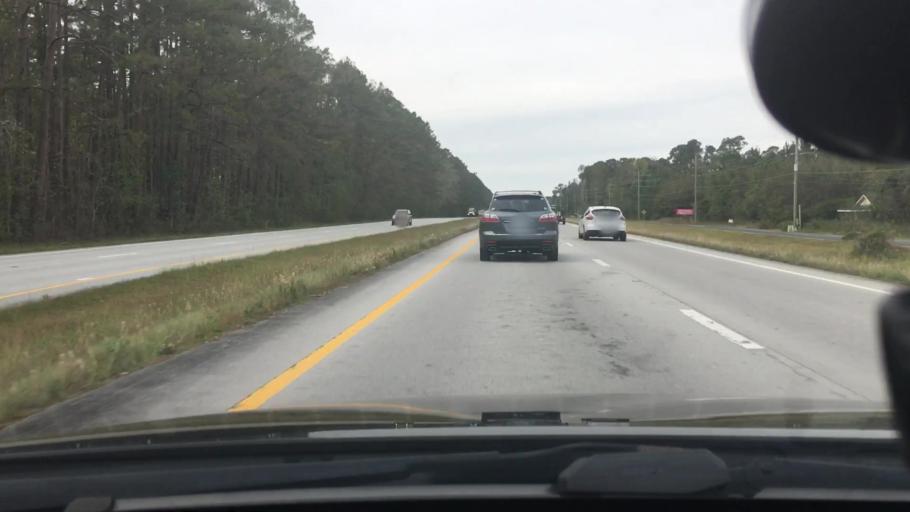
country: US
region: North Carolina
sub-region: Craven County
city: Neuse Forest
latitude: 34.9777
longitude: -76.9759
